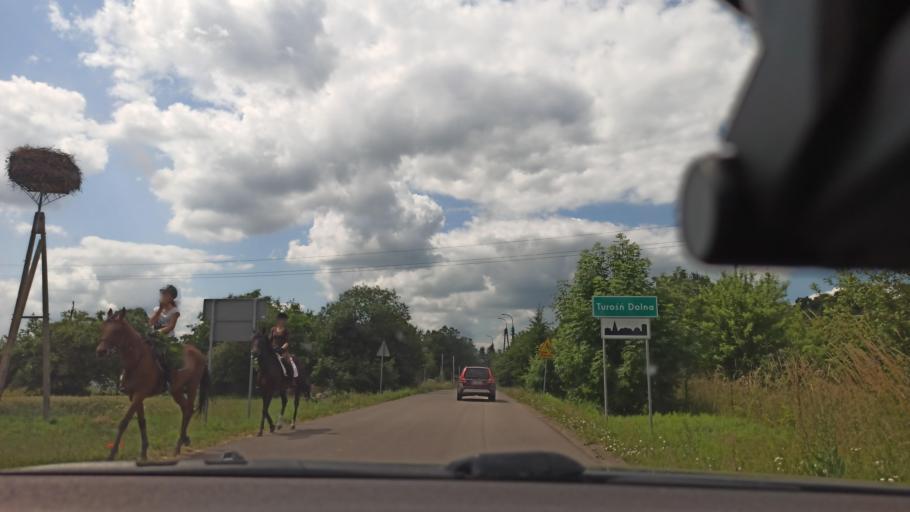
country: PL
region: Podlasie
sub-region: Powiat bialostocki
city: Turosn Koscielna
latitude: 53.0192
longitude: 23.0099
